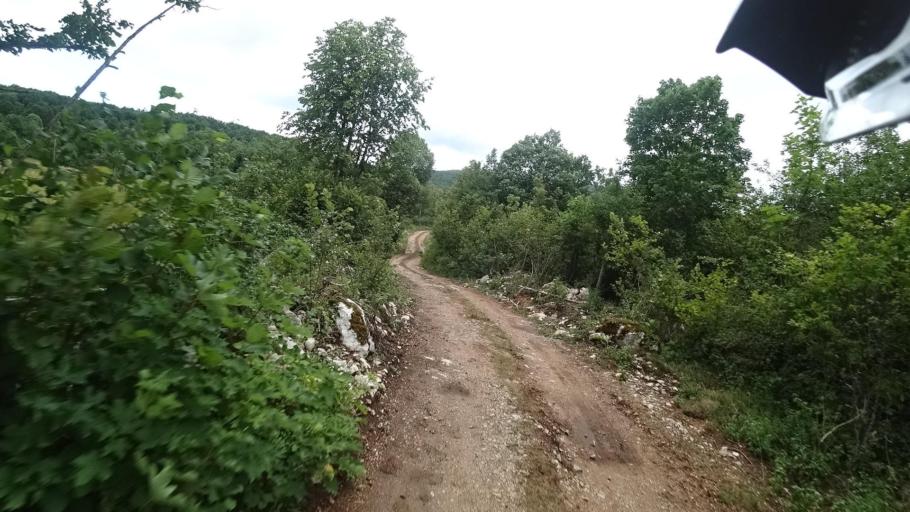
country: HR
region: Licko-Senjska
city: Jezerce
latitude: 44.7743
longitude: 15.4837
